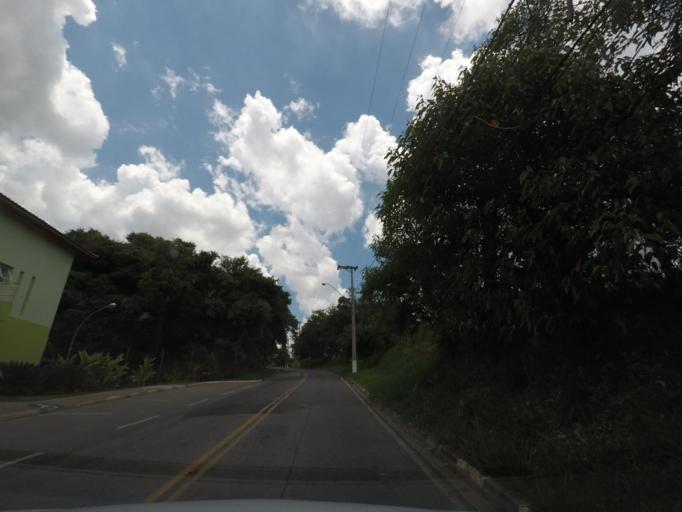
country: BR
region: Sao Paulo
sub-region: Vinhedo
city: Vinhedo
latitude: -23.0486
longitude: -46.9696
